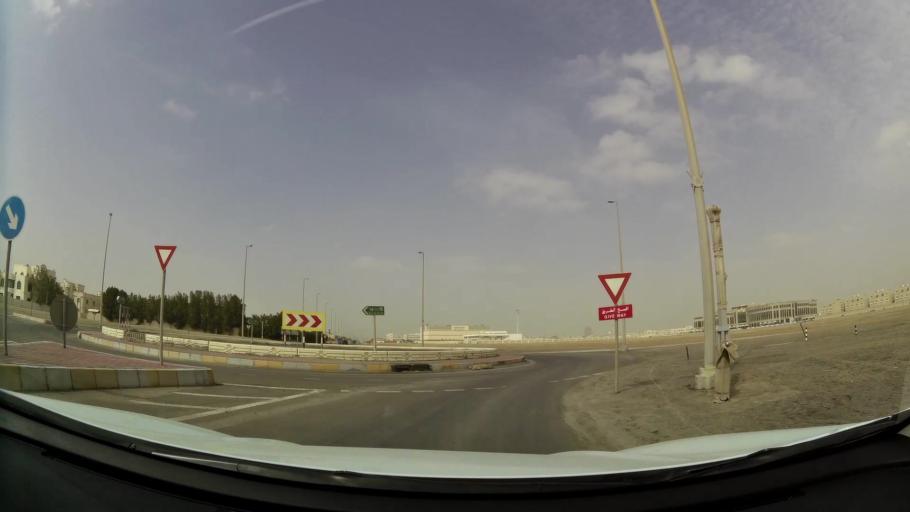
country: AE
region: Abu Dhabi
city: Abu Dhabi
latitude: 24.4078
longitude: 54.5680
